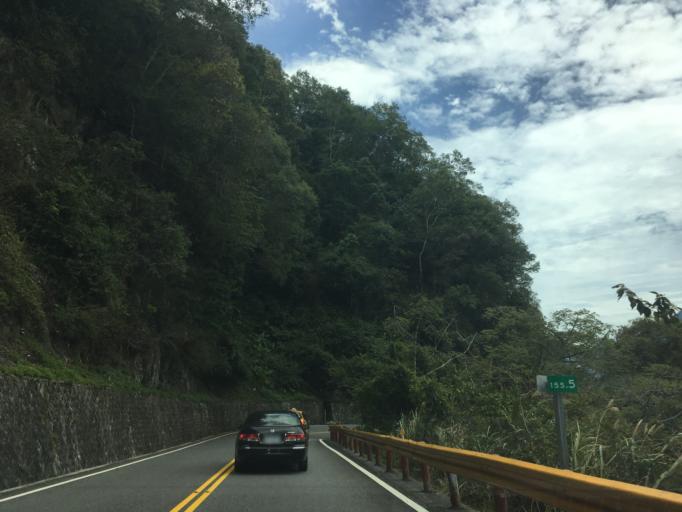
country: TW
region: Taiwan
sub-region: Hualien
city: Hualian
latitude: 24.1982
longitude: 121.4618
